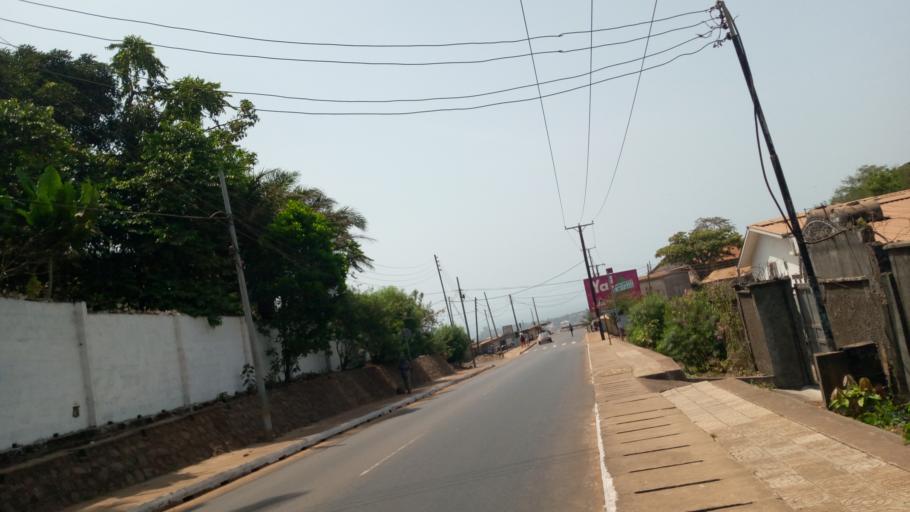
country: SL
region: Western Area
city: Freetown
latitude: 8.4803
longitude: -13.2646
